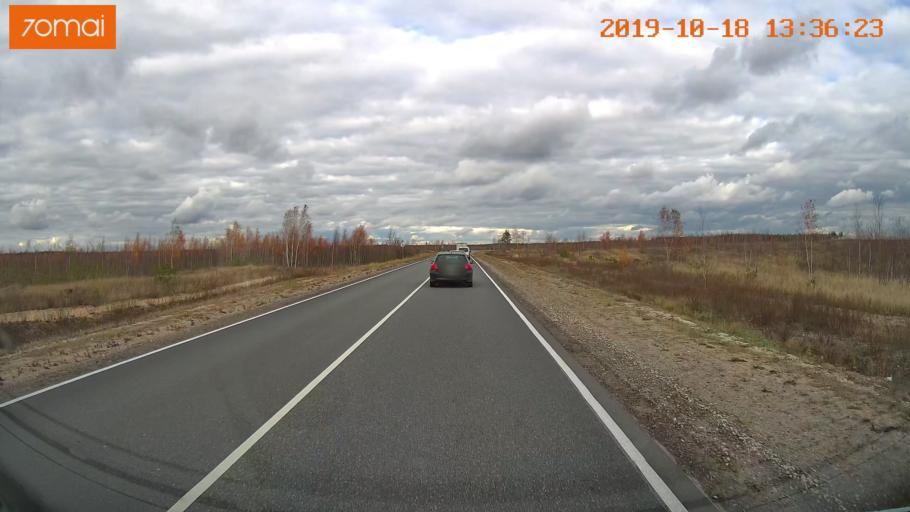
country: RU
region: Rjazan
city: Solotcha
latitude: 54.8696
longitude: 39.9843
